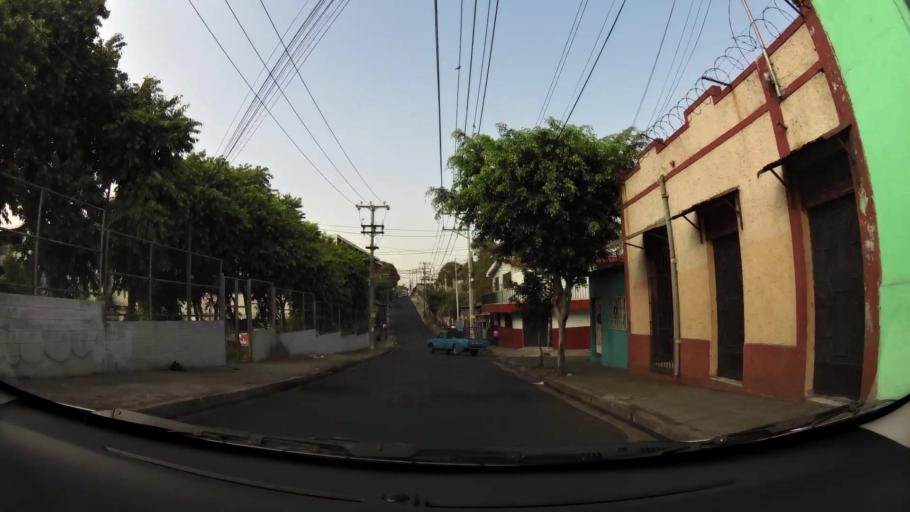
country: SV
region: San Salvador
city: San Salvador
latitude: 13.6973
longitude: -89.1832
